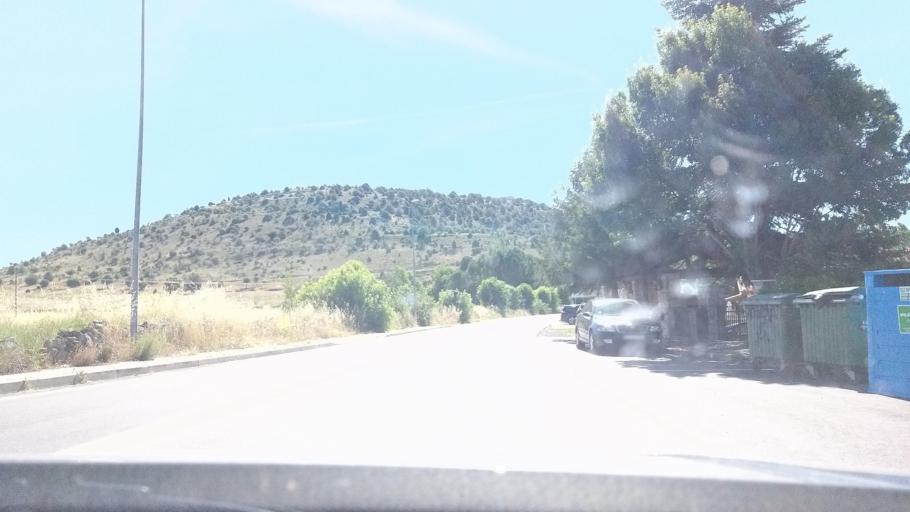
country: ES
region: Castille and Leon
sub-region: Provincia de Segovia
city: Pedraza
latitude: 41.1424
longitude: -3.8256
